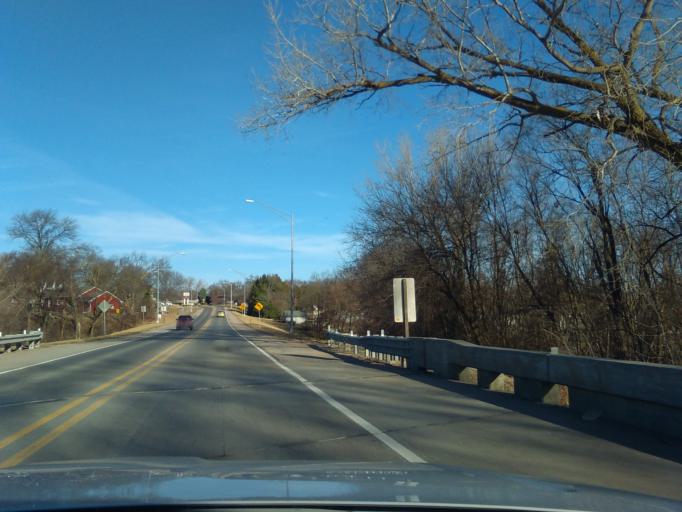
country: US
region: Nebraska
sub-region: Seward County
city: Seward
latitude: 40.9045
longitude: -97.0889
